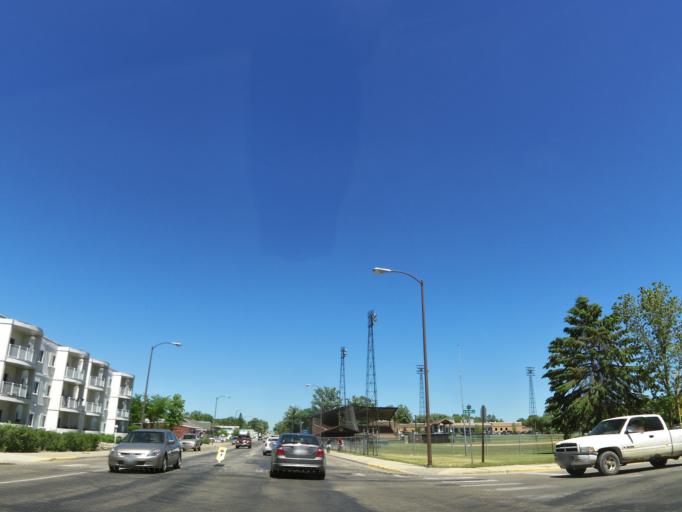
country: US
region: Minnesota
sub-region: Becker County
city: Detroit Lakes
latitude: 46.8075
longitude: -95.8459
